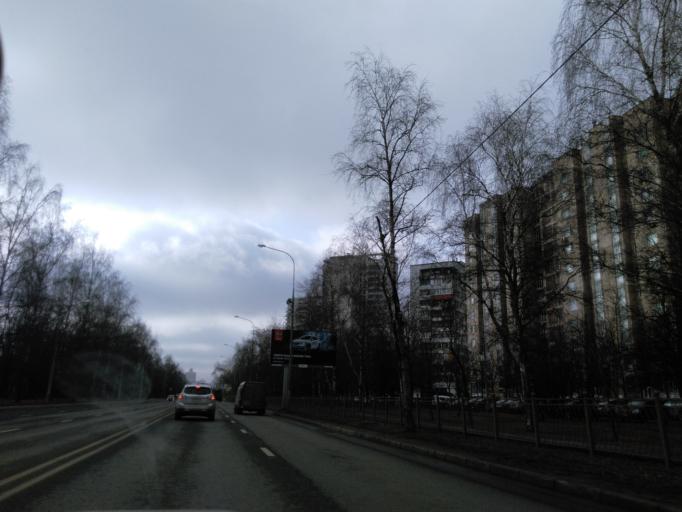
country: RU
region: Moskovskaya
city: Levoberezhnyy
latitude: 55.8569
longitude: 37.4503
